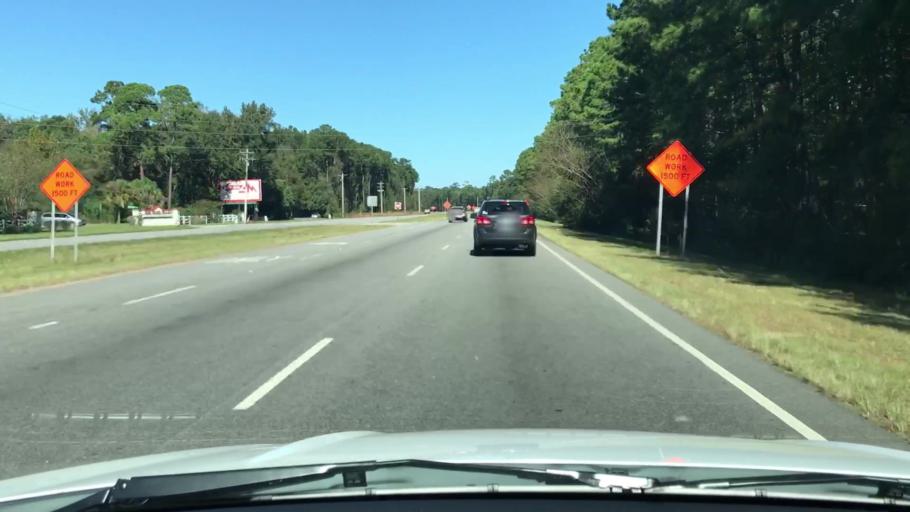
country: US
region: South Carolina
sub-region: Beaufort County
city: Bluffton
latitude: 32.3264
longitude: -80.9310
